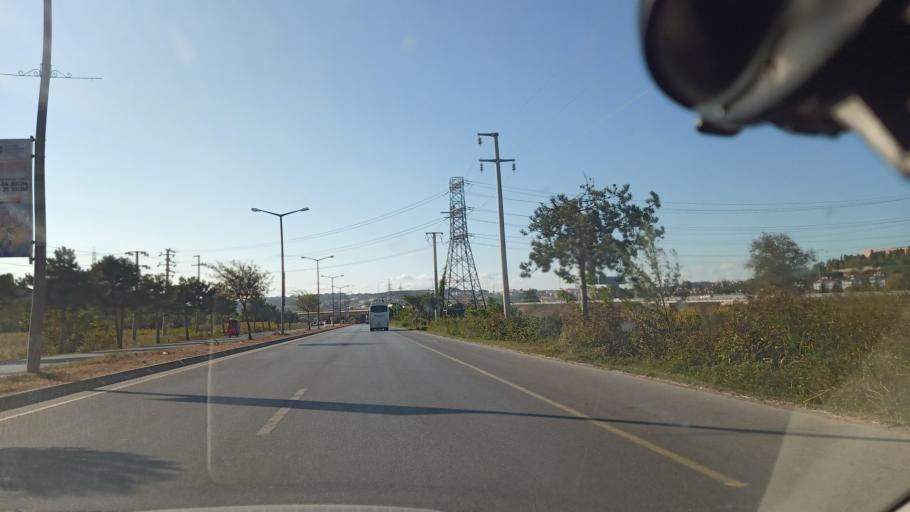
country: TR
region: Sakarya
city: Kazimpasa
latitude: 40.8419
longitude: 30.3372
